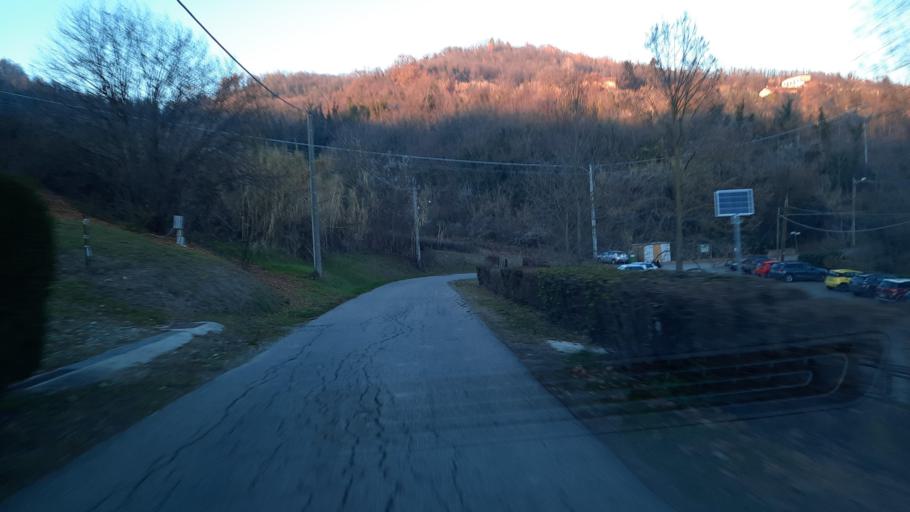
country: IT
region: Piedmont
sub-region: Provincia di Alessandria
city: Camino
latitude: 45.1584
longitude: 8.2690
